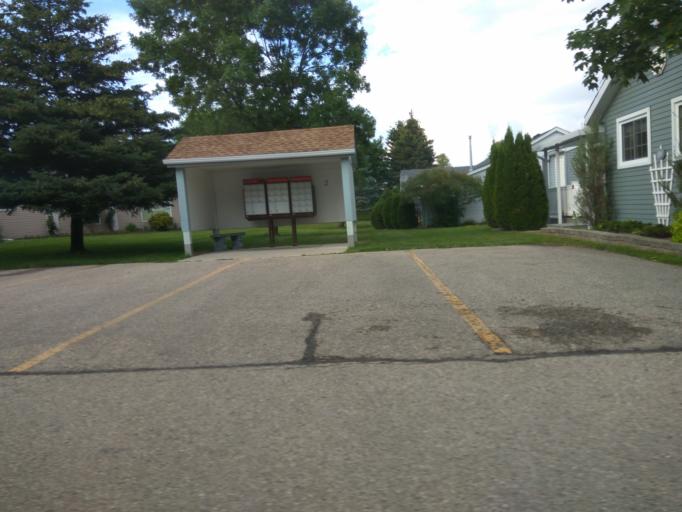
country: CA
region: Ontario
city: Kitchener
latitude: 43.3731
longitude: -80.6934
